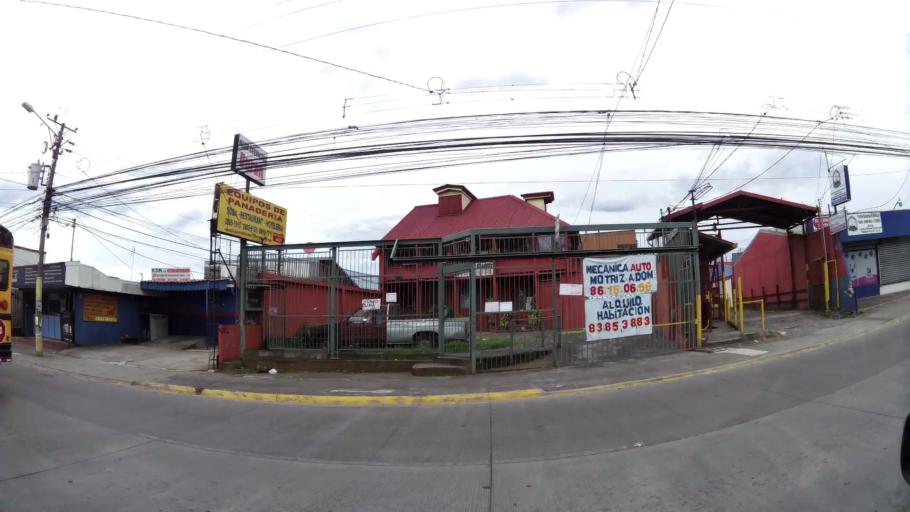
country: CR
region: San Jose
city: Purral
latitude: 9.9595
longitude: -84.0383
